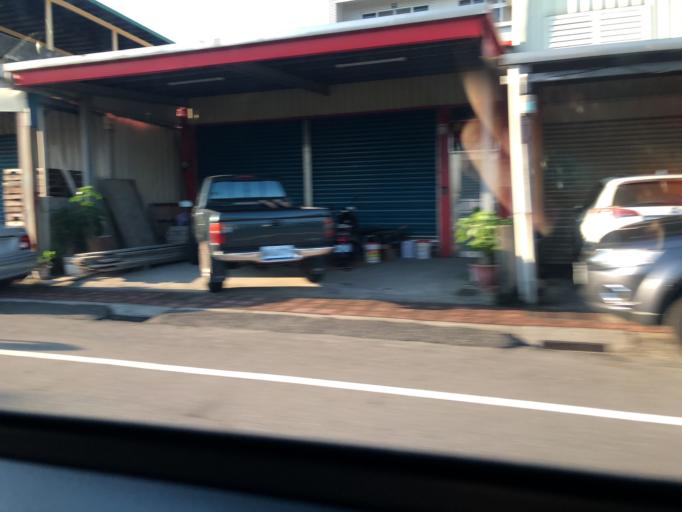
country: TW
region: Taiwan
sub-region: Yilan
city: Yilan
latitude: 24.7502
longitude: 121.7730
